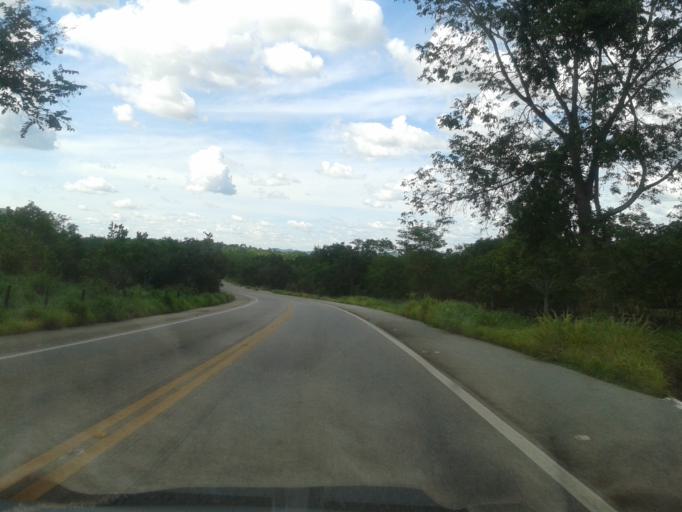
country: BR
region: Goias
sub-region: Itapuranga
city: Itapuranga
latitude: -15.5441
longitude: -50.2887
